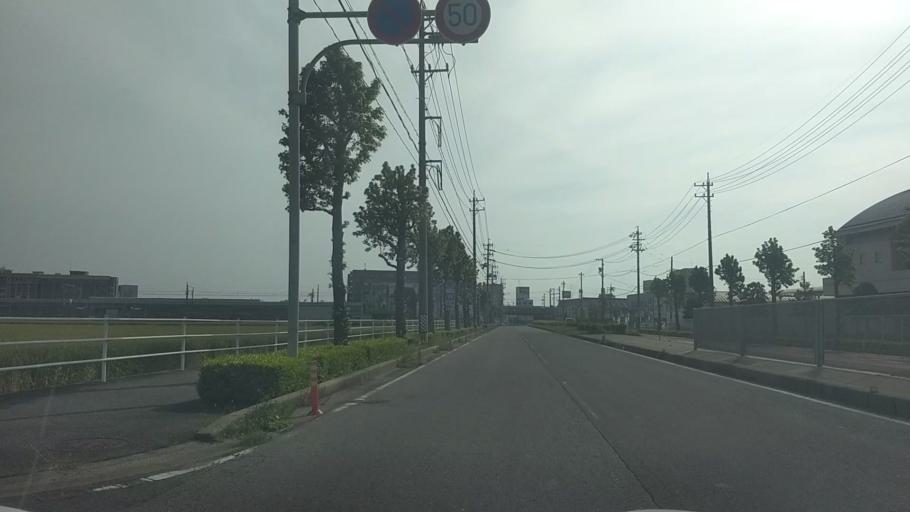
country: JP
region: Aichi
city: Anjo
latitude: 34.9607
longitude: 137.0636
